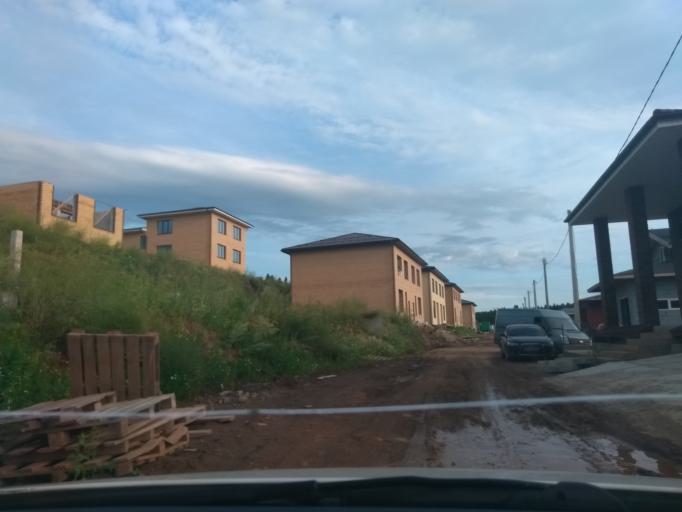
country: RU
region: Perm
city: Perm
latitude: 57.9998
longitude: 56.3216
